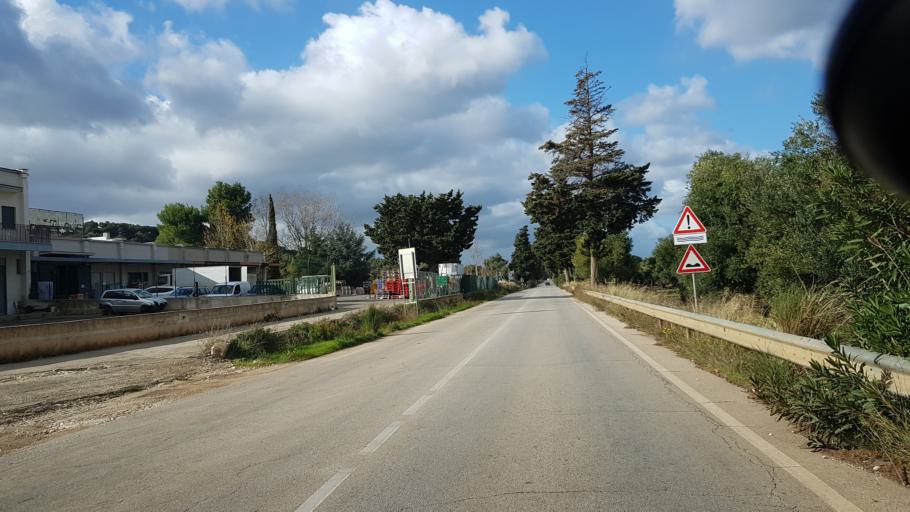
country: IT
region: Apulia
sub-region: Provincia di Brindisi
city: Ostuni
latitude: 40.7491
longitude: 17.5543
